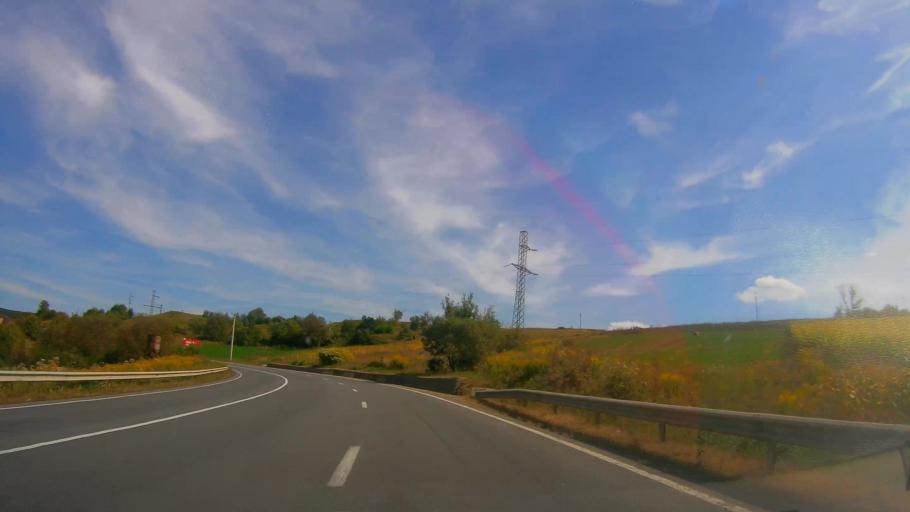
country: RO
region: Mures
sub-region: Municipiul Sighisoara
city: Sighisoara
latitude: 46.2665
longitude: 24.7640
